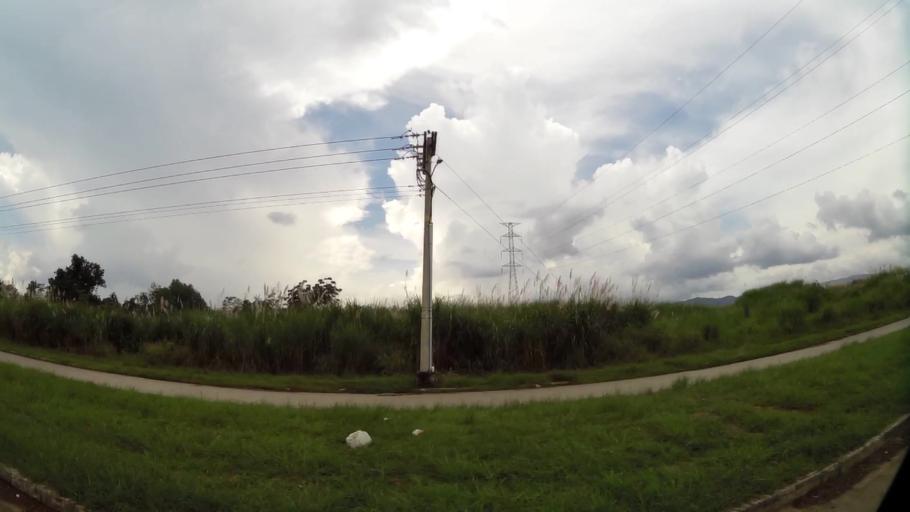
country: PA
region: Panama
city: Cabra Numero Uno
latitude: 9.1135
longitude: -79.3202
